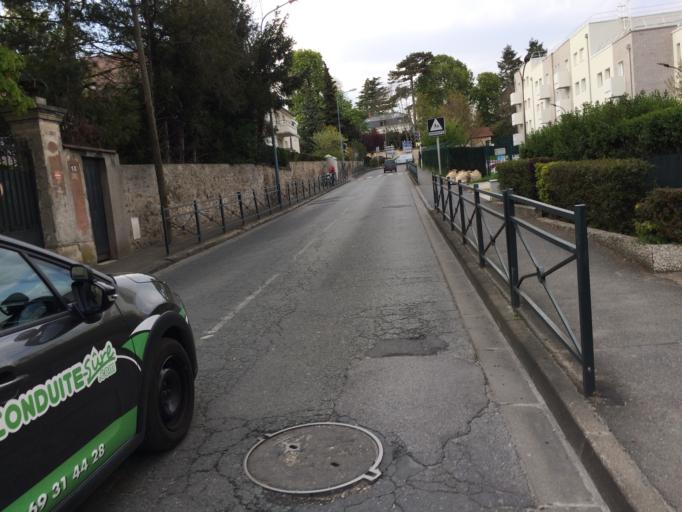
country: FR
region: Ile-de-France
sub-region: Departement de l'Essonne
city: Villebon-sur-Yvette
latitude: 48.7100
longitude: 2.2463
